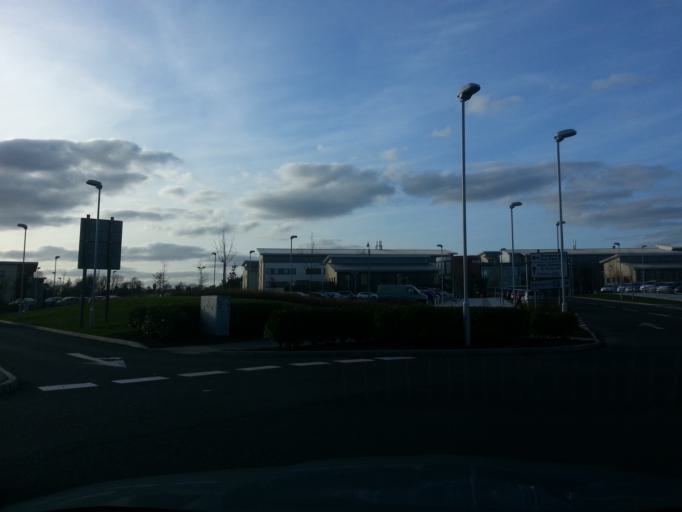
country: GB
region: Northern Ireland
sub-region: Fermanagh District
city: Enniskillen
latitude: 54.3645
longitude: -7.6373
